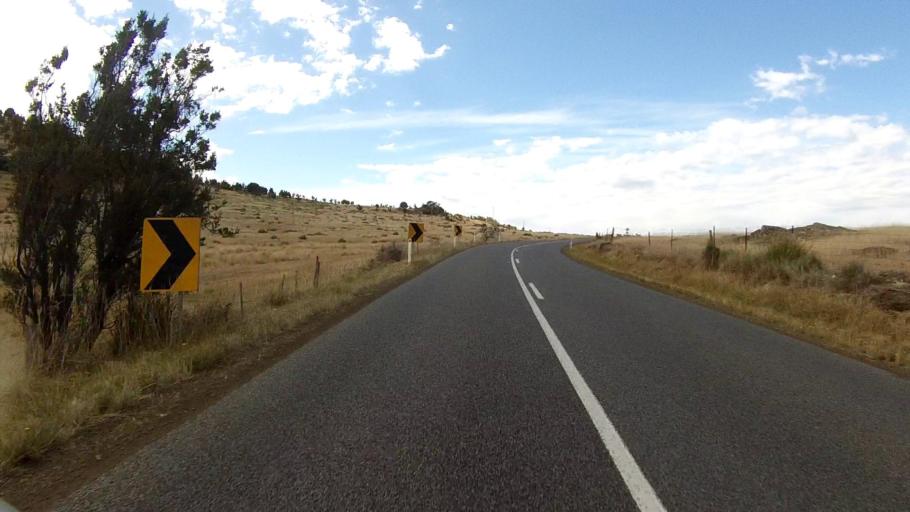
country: AU
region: Tasmania
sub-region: Sorell
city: Sorell
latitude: -42.1924
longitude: 148.0606
